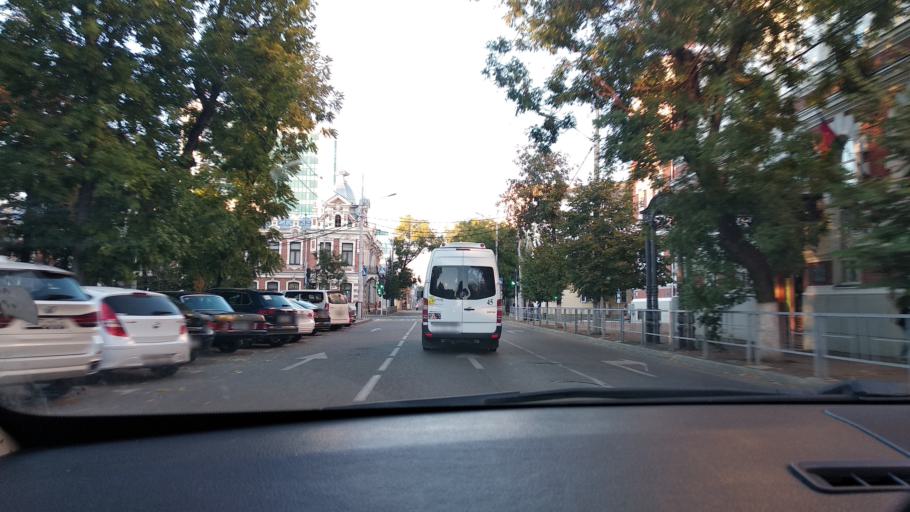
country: RU
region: Krasnodarskiy
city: Krasnodar
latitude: 45.0244
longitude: 38.9726
